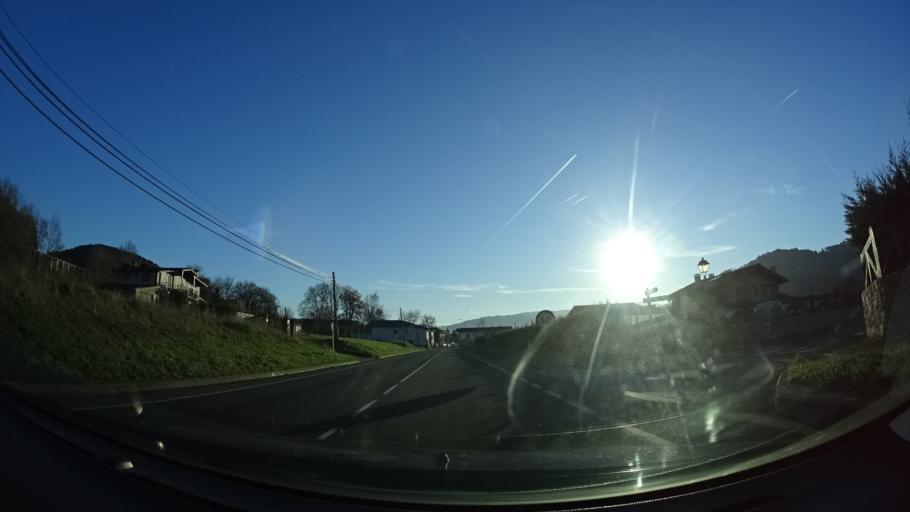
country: ES
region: Basque Country
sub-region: Bizkaia
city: Forua
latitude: 43.3263
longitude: -2.6665
